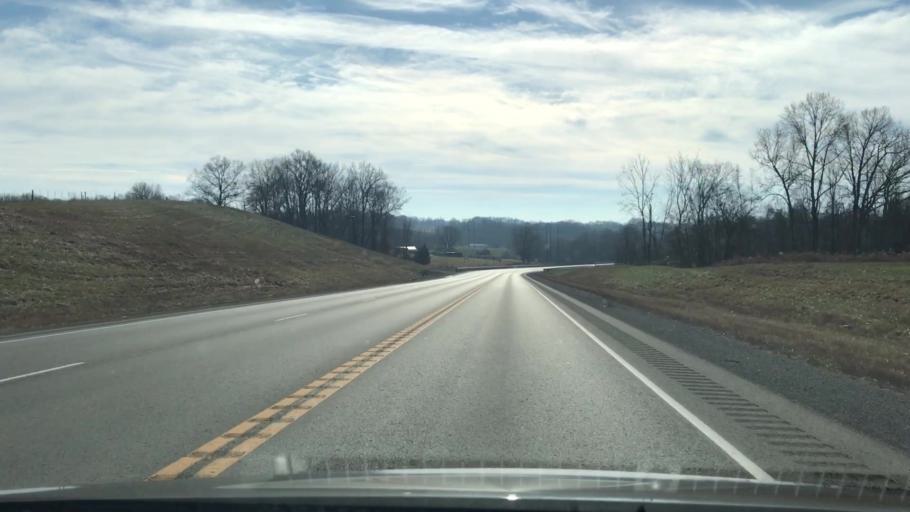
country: US
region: Kentucky
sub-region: Monroe County
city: Tompkinsville
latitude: 36.8452
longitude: -85.6758
